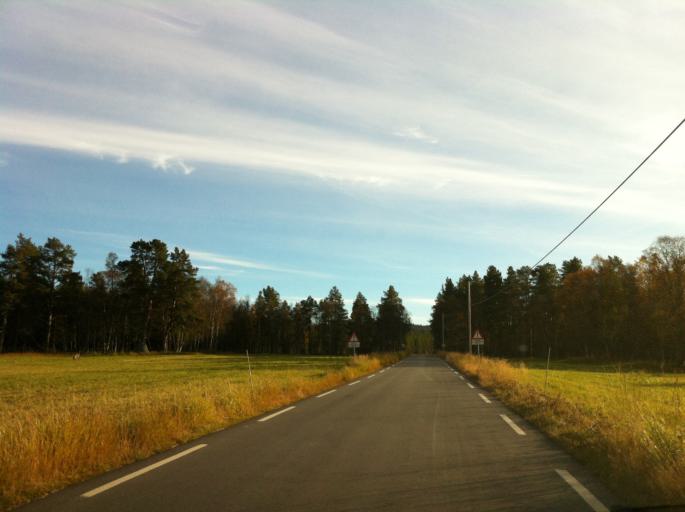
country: NO
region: Hedmark
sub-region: Engerdal
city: Engerdal
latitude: 62.1588
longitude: 11.9468
